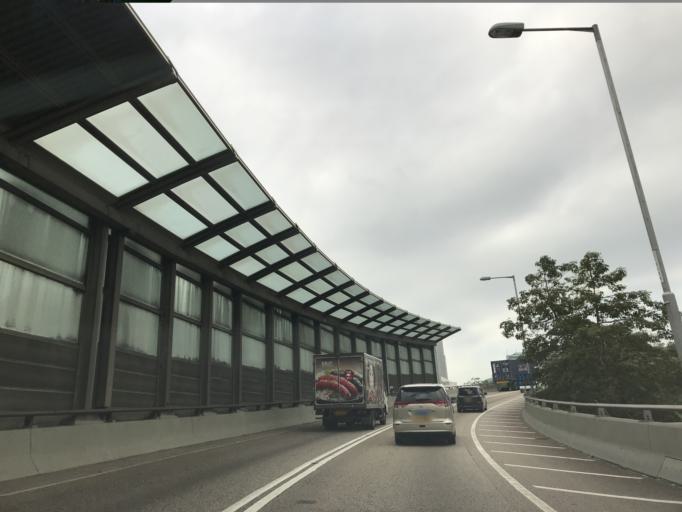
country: HK
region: Sha Tin
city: Sha Tin
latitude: 22.3788
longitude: 114.1857
